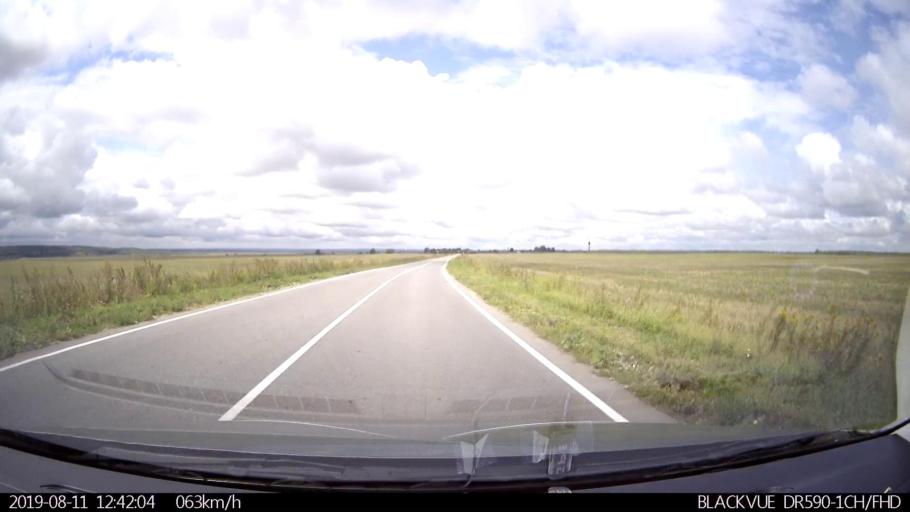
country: RU
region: Ulyanovsk
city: Ignatovka
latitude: 53.8431
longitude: 47.7559
